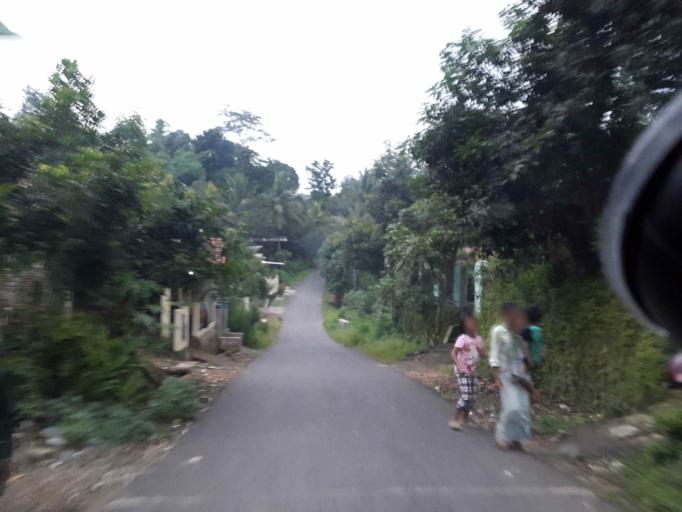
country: ID
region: Central Java
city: Randudongkal
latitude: -7.0725
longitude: 109.3299
